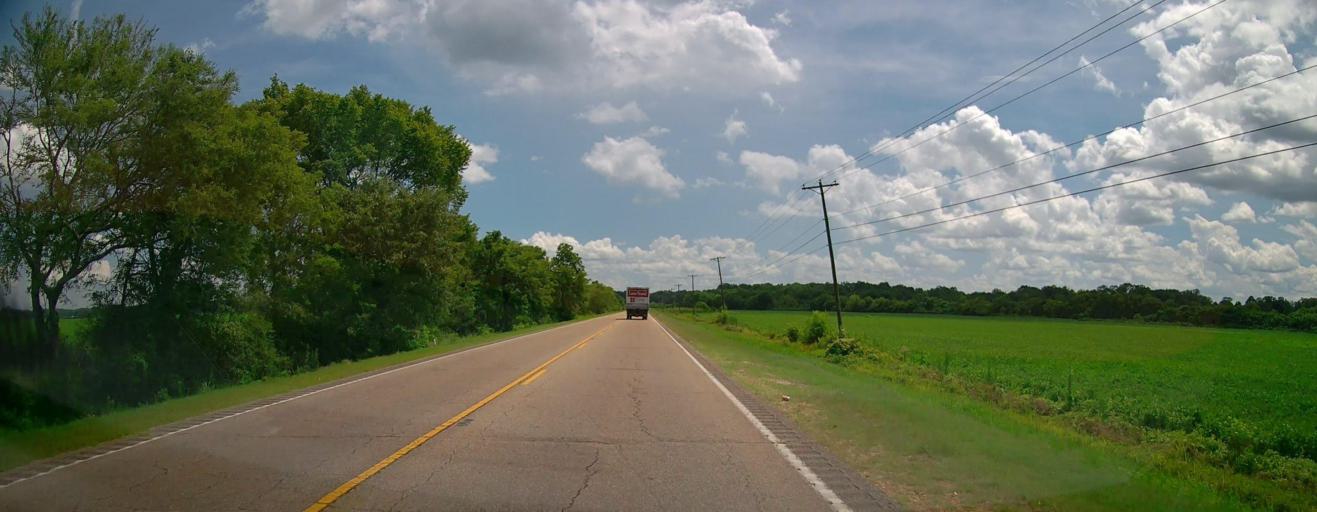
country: US
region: Mississippi
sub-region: Lee County
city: Shannon
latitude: 34.1463
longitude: -88.7194
